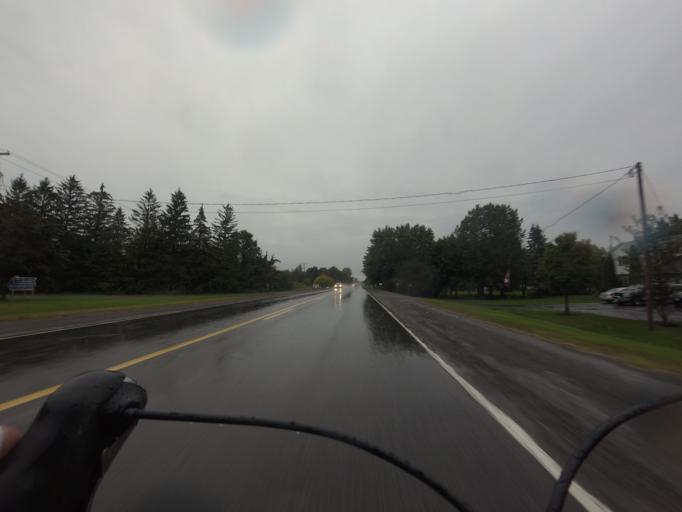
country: CA
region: Ontario
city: Bells Corners
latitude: 45.1804
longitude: -75.7198
